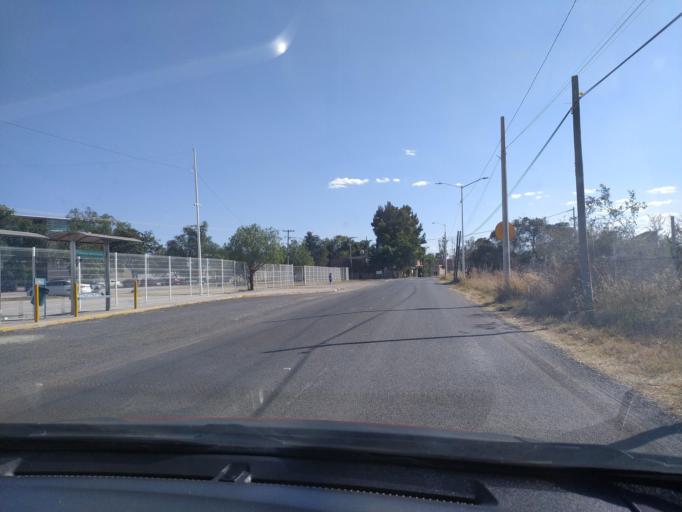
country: LA
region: Oudomxai
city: Muang La
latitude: 21.0352
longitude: 101.8385
